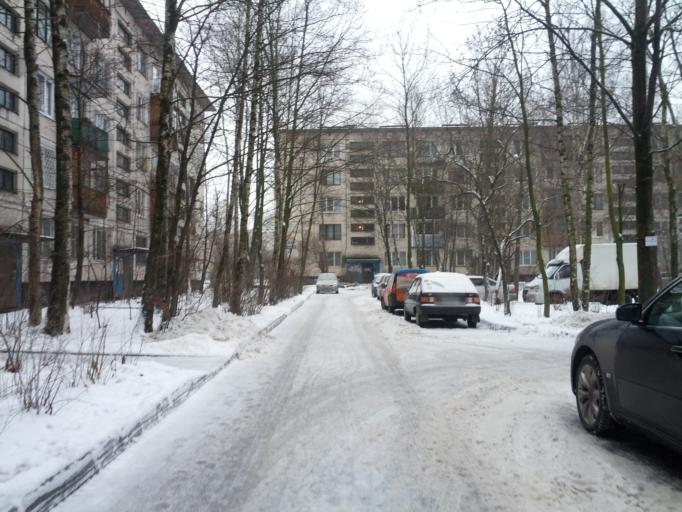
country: RU
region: St.-Petersburg
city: Krasnogvargeisky
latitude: 59.9092
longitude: 30.4758
